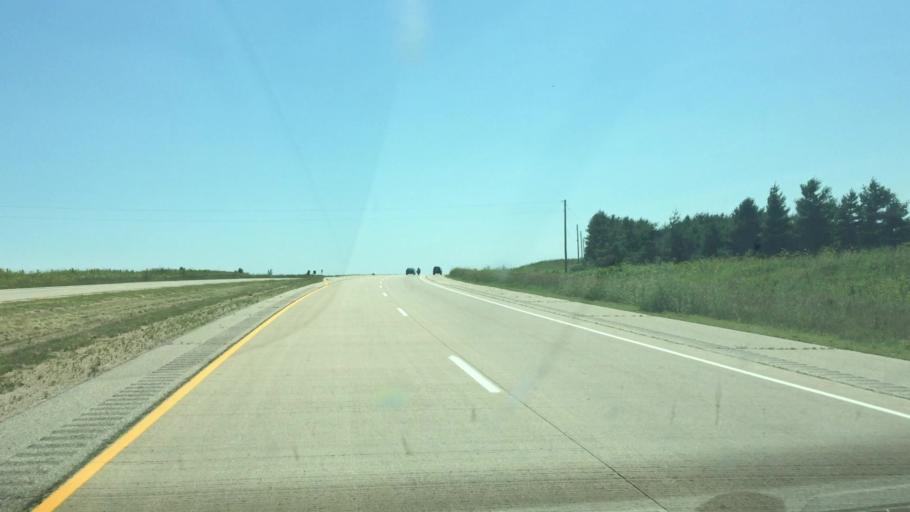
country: US
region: Wisconsin
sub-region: Iowa County
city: Mineral Point
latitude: 42.7975
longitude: -90.2799
